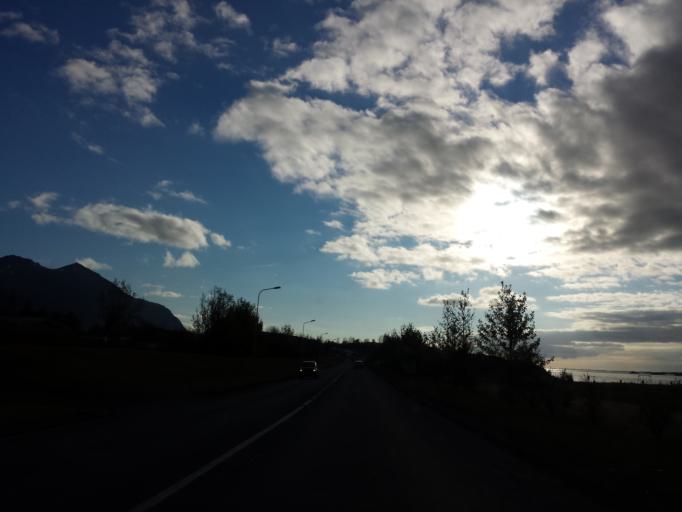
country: IS
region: West
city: Borgarnes
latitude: 64.5529
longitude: -21.9061
